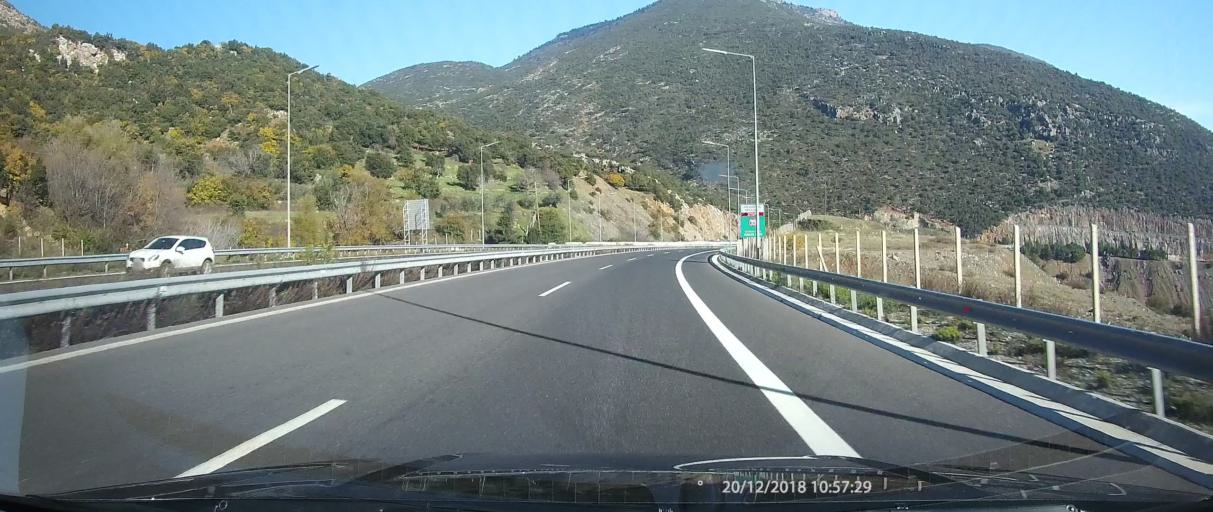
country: GR
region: Peloponnese
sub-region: Nomos Arkadias
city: Tripoli
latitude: 37.6810
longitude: 22.4886
